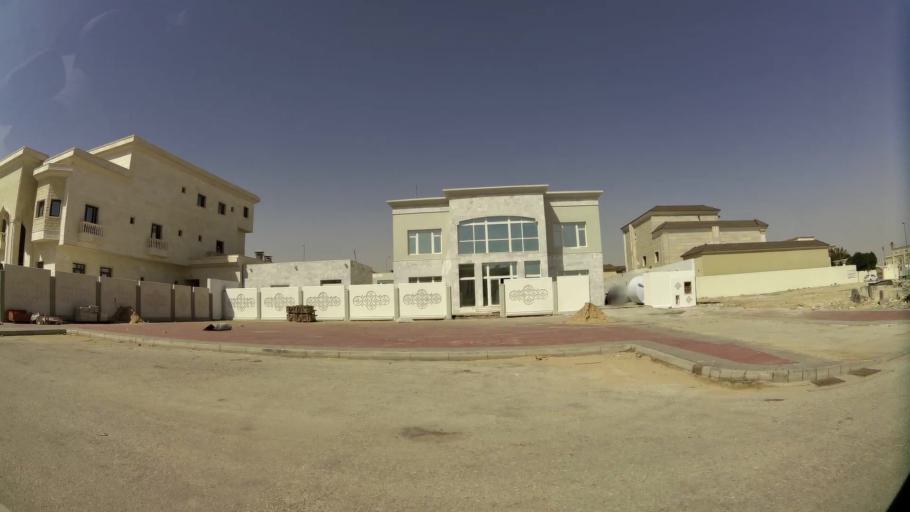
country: QA
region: Baladiyat ad Dawhah
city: Doha
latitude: 25.3557
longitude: 51.4968
